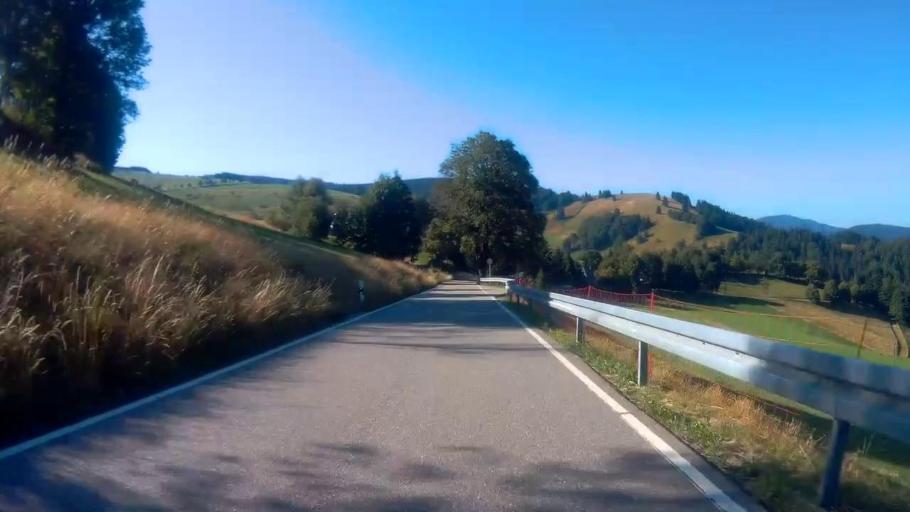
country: DE
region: Baden-Wuerttemberg
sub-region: Freiburg Region
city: Horben
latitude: 47.8950
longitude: 7.8752
